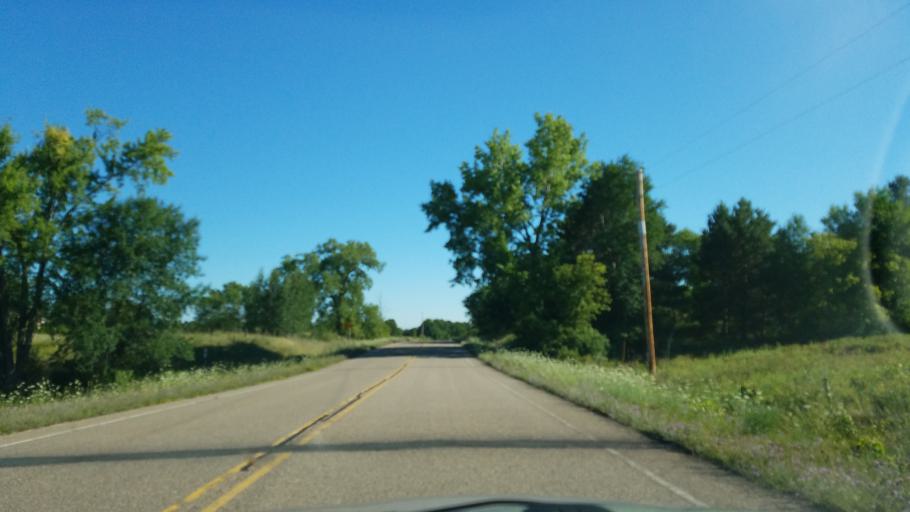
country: US
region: Wisconsin
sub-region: Saint Croix County
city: Somerset
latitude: 45.1100
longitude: -92.7268
